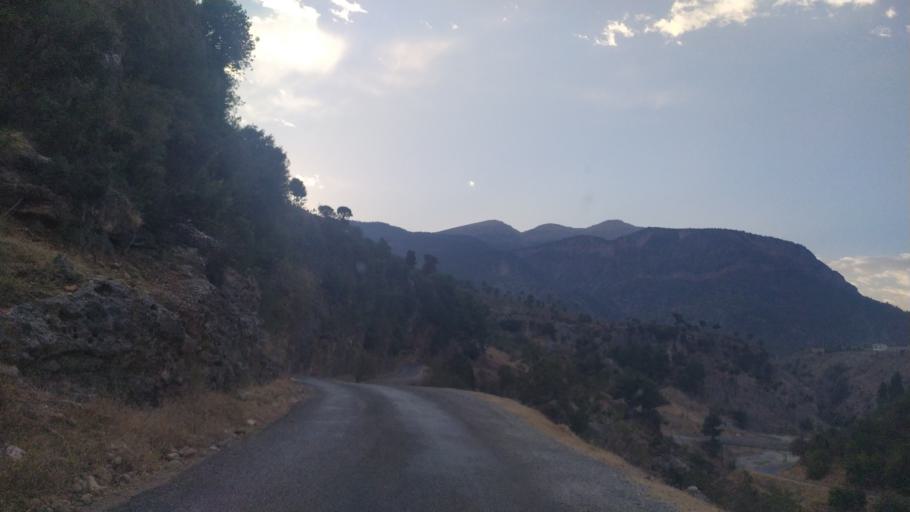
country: TR
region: Mersin
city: Camliyayla
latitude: 37.2377
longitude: 34.7163
